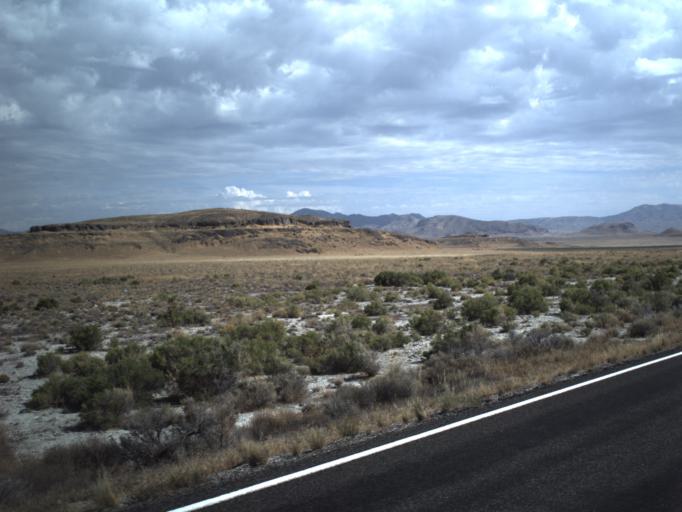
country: US
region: Utah
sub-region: Tooele County
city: Wendover
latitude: 41.4199
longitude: -113.9045
